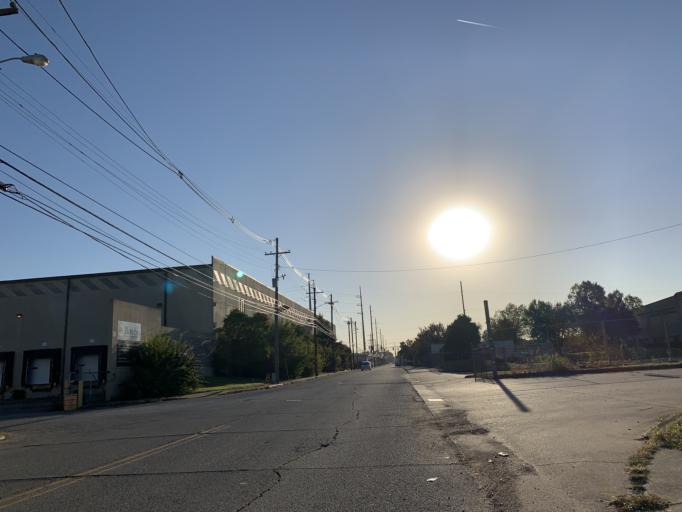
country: US
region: Kentucky
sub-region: Jefferson County
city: Louisville
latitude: 38.2410
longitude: -85.7747
